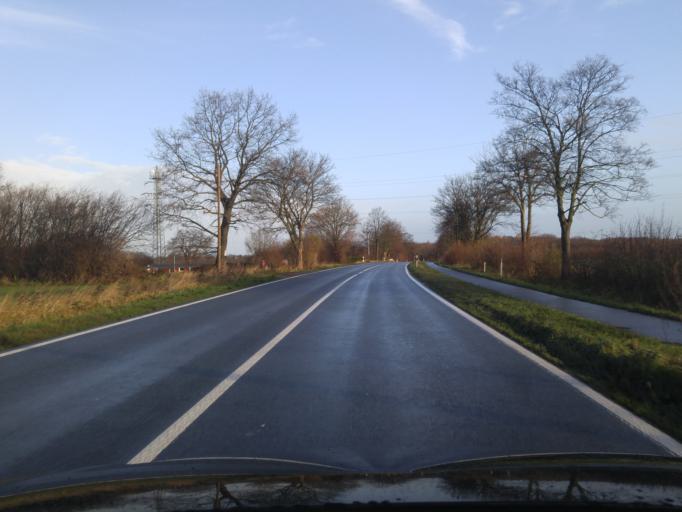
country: DE
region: Schleswig-Holstein
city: Ratekau
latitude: 53.9536
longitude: 10.7534
